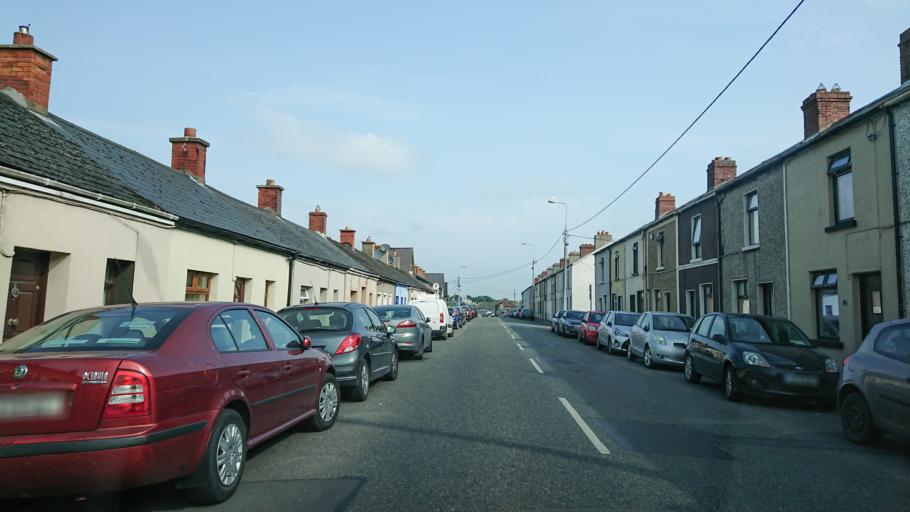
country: IE
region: Munster
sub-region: Waterford
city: Waterford
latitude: 52.2563
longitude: -7.1217
